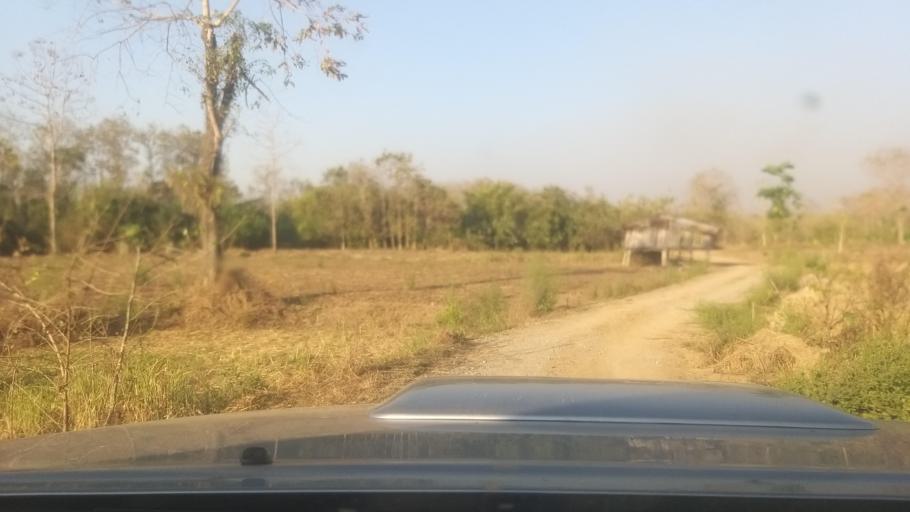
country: TH
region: Phrae
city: Nong Muang Khai
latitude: 18.2724
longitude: 100.0243
